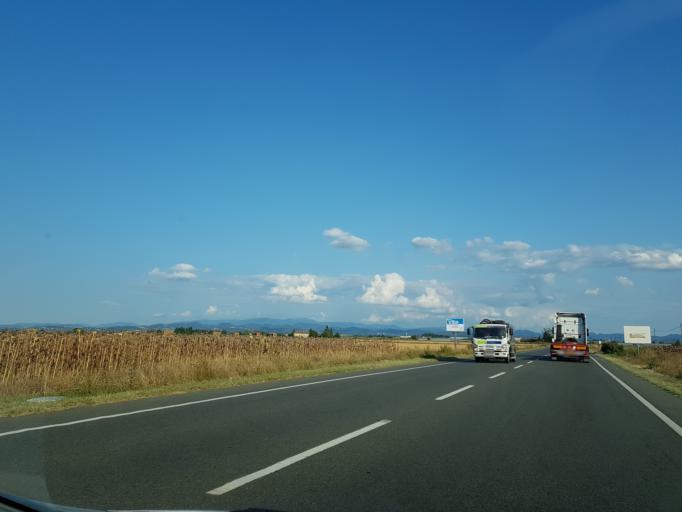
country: IT
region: Piedmont
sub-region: Provincia di Alessandria
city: Pozzolo Formigaro
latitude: 44.8181
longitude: 8.7557
